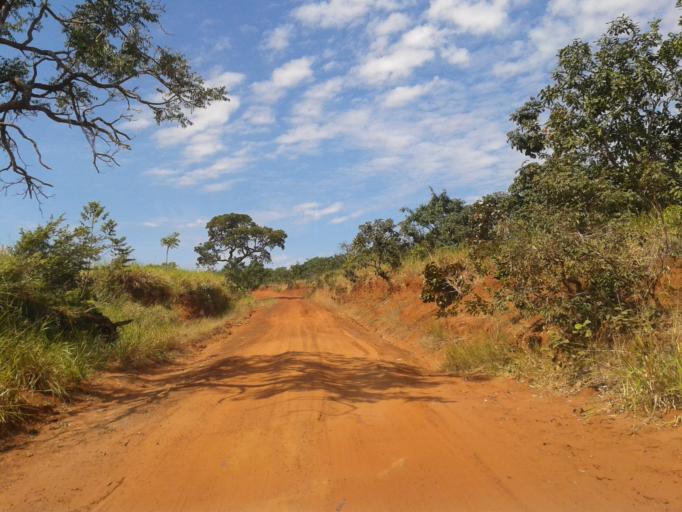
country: BR
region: Minas Gerais
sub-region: Campina Verde
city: Campina Verde
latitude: -19.4016
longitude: -49.7575
